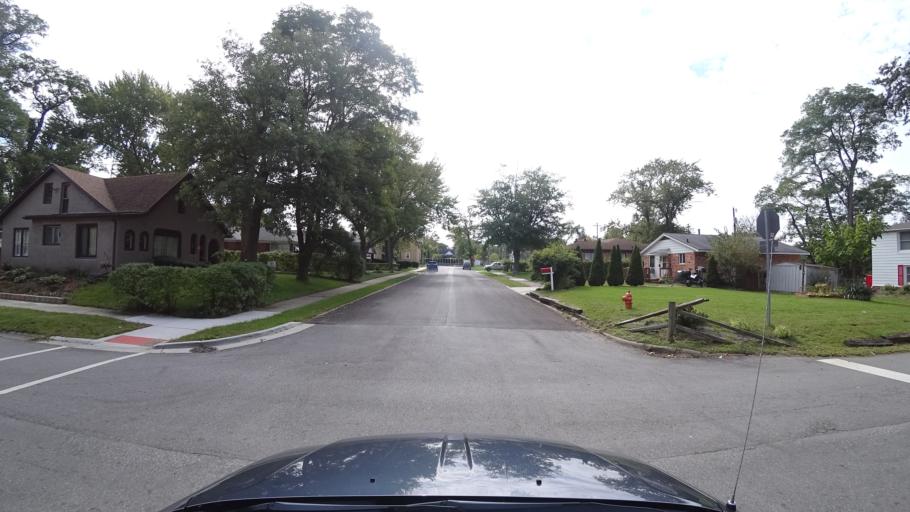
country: US
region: Indiana
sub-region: LaPorte County
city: Trail Creek
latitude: 41.7106
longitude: -86.8728
